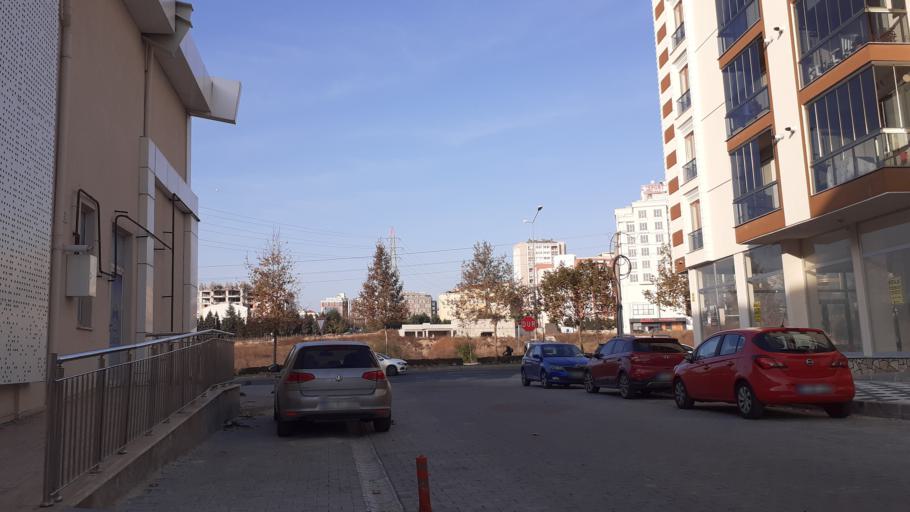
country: TR
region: Tekirdag
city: Corlu
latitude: 41.1488
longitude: 27.8284
